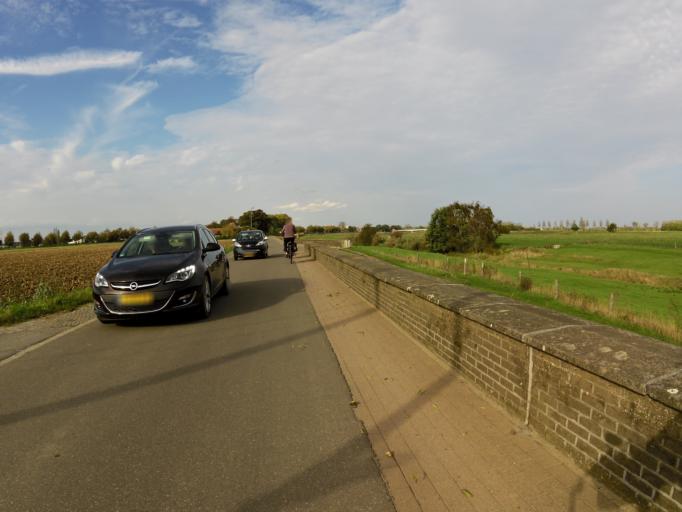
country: BE
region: Flanders
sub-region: Provincie Limburg
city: Maaseik
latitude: 51.0834
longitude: 5.7950
